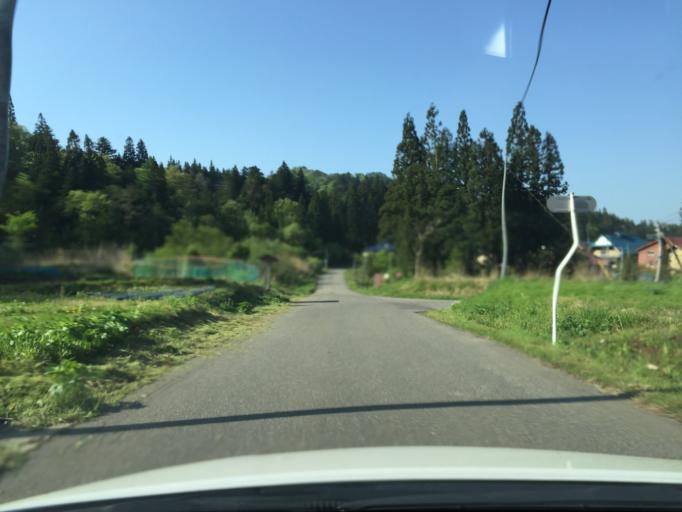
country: JP
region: Fukushima
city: Kitakata
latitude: 37.6746
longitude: 139.6482
